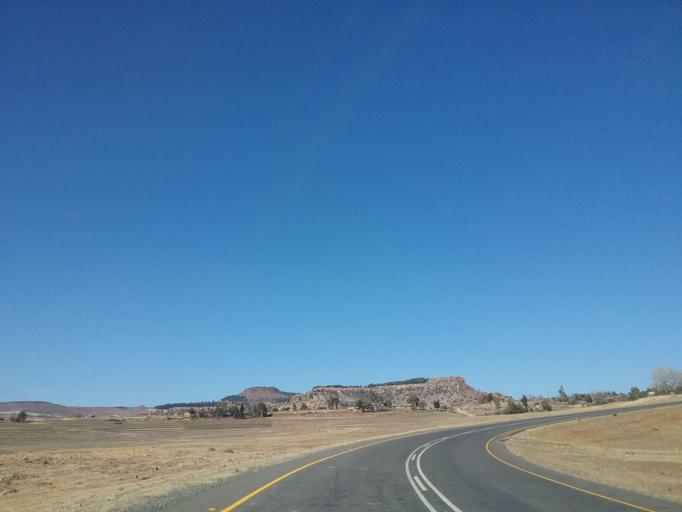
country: LS
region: Maseru
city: Nako
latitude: -29.4607
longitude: 27.6471
